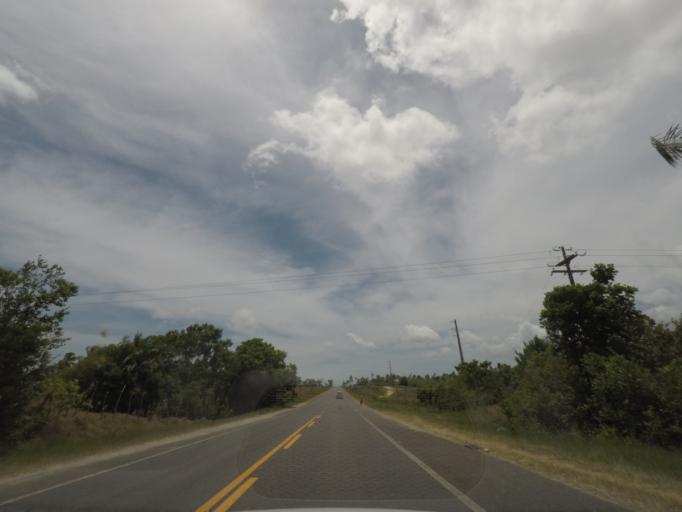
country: BR
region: Bahia
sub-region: Conde
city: Conde
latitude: -11.8197
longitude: -37.6354
